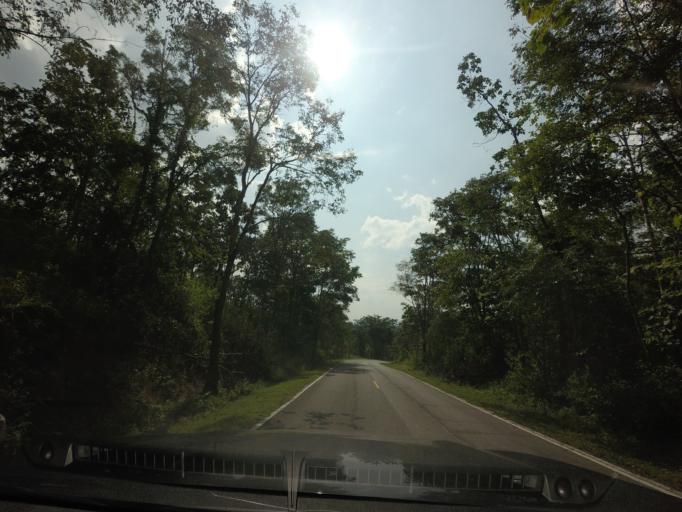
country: TH
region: Uttaradit
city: Ban Khok
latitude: 18.1675
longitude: 101.0825
